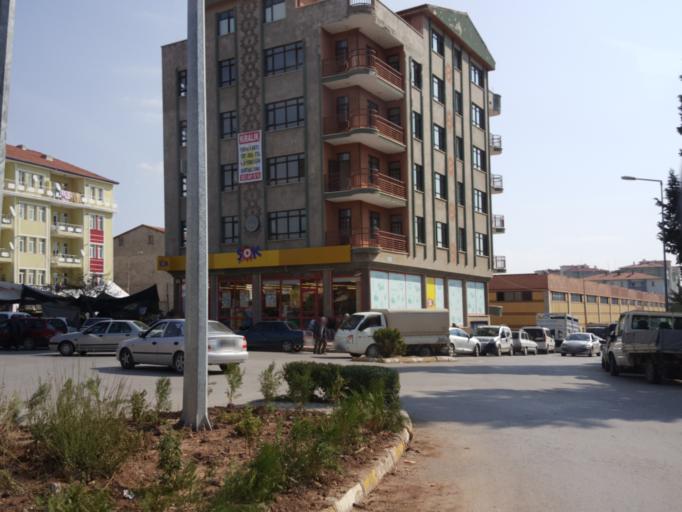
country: TR
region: Tokat
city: Zile
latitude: 40.2988
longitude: 35.8872
